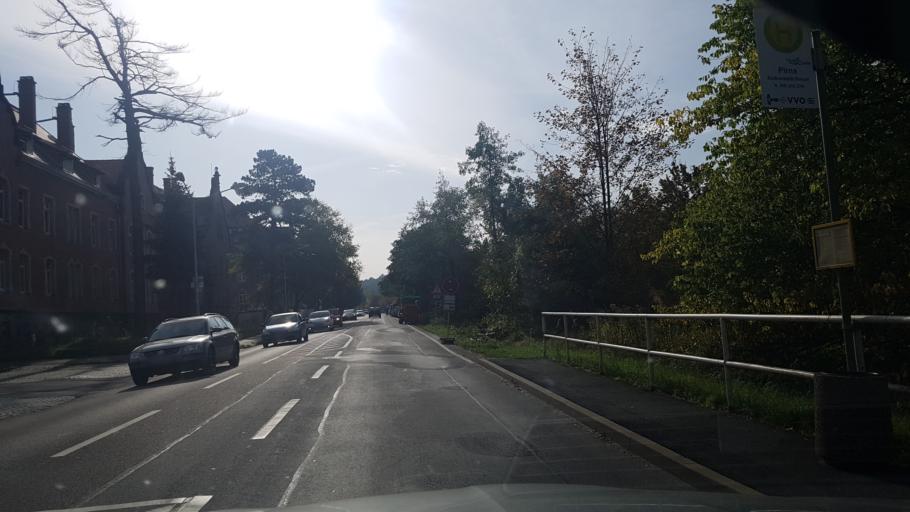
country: DE
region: Saxony
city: Pirna
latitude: 50.9410
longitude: 13.9441
